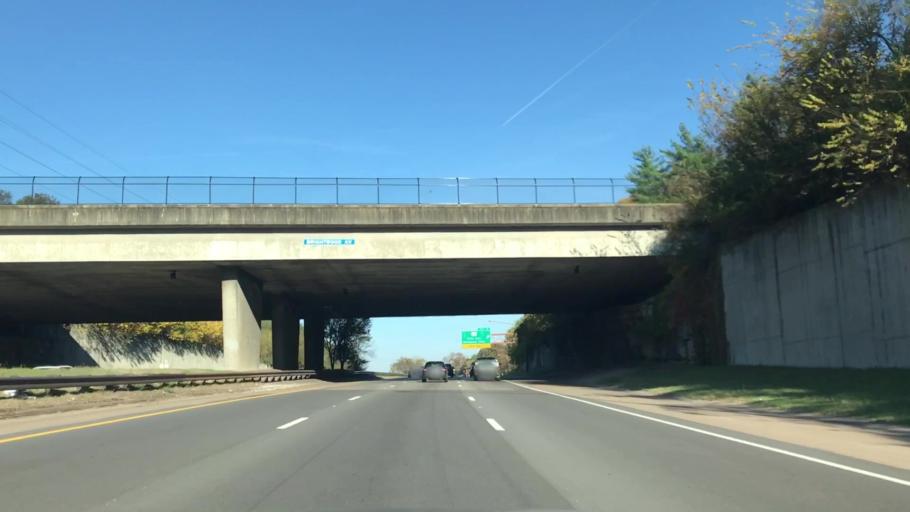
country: US
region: Tennessee
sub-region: Davidson County
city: Oak Hill
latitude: 36.1156
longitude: -86.8000
